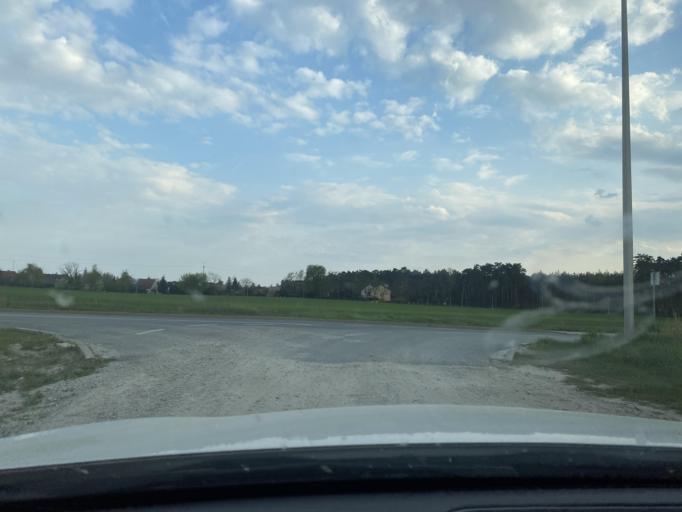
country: PL
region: Lower Silesian Voivodeship
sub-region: Powiat wroclawski
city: Mirkow
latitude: 51.1538
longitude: 17.1563
